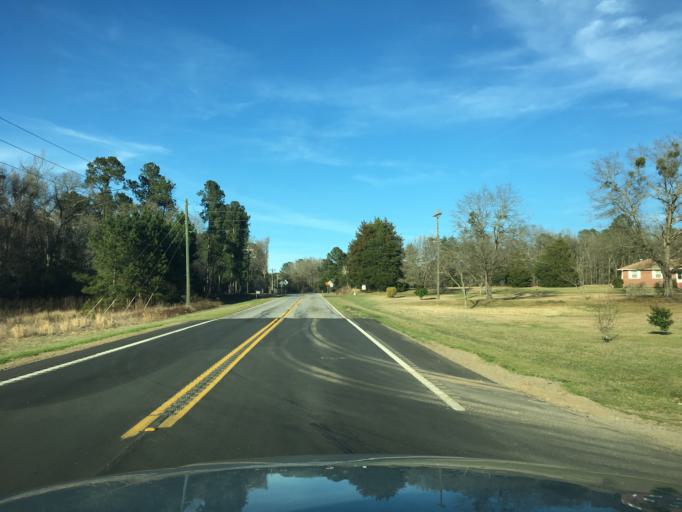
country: US
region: South Carolina
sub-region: Edgefield County
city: Johnston
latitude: 33.7312
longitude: -81.6516
